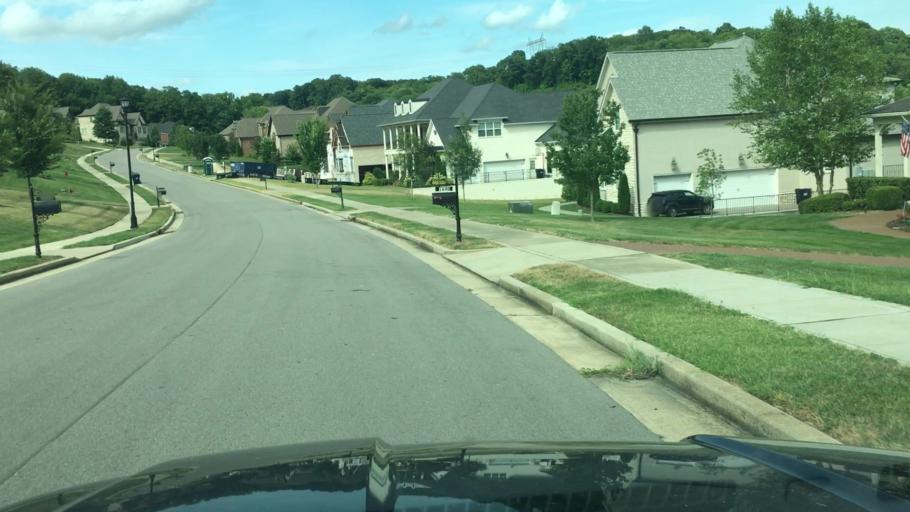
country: US
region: Tennessee
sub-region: Williamson County
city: Brentwood Estates
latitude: 35.9726
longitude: -86.8206
